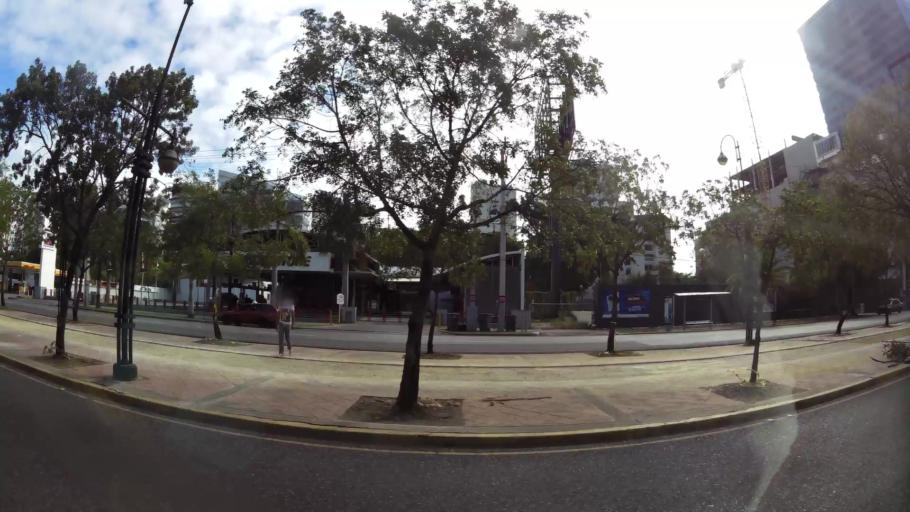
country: DO
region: Nacional
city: La Julia
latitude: 18.4735
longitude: -69.9422
